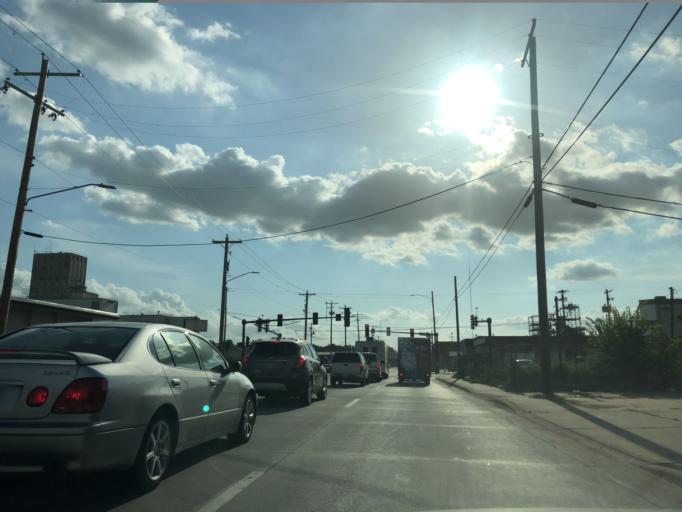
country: US
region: Kansas
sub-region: Sedgwick County
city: Wichita
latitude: 37.7081
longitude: -97.3269
